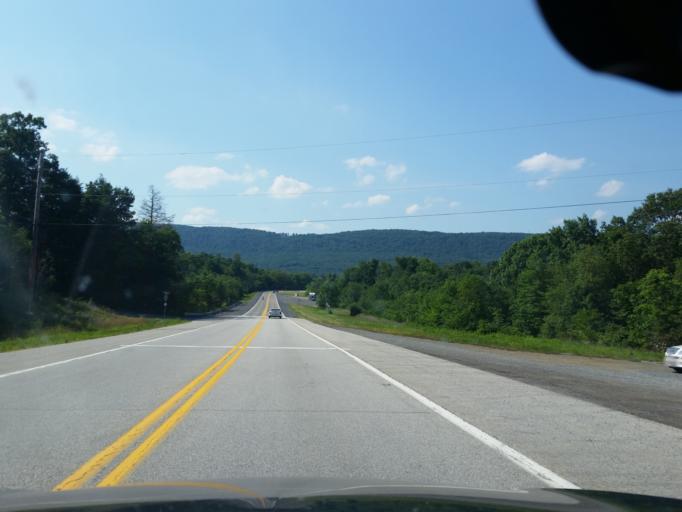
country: US
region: Pennsylvania
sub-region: Cumberland County
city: Mechanicsburg
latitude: 40.2751
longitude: -77.0466
